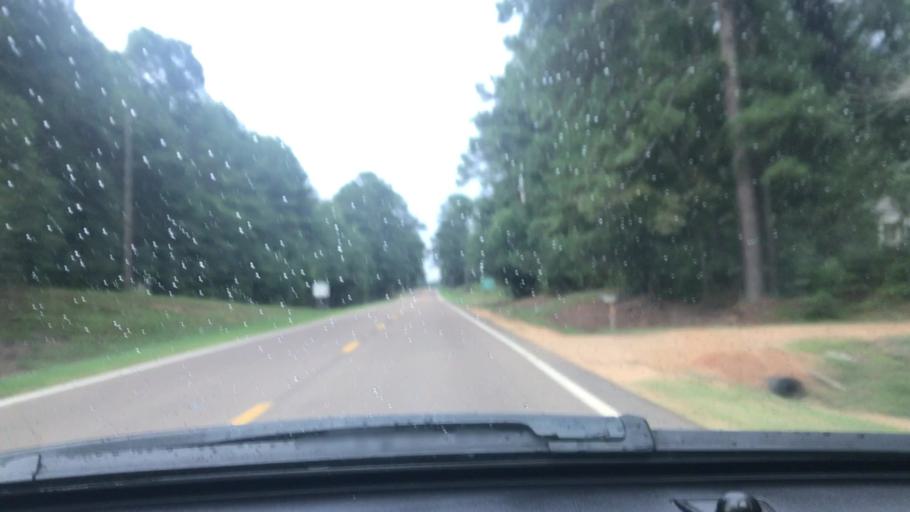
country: US
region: Mississippi
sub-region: Pike County
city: Summit
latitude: 31.3496
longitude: -90.5997
